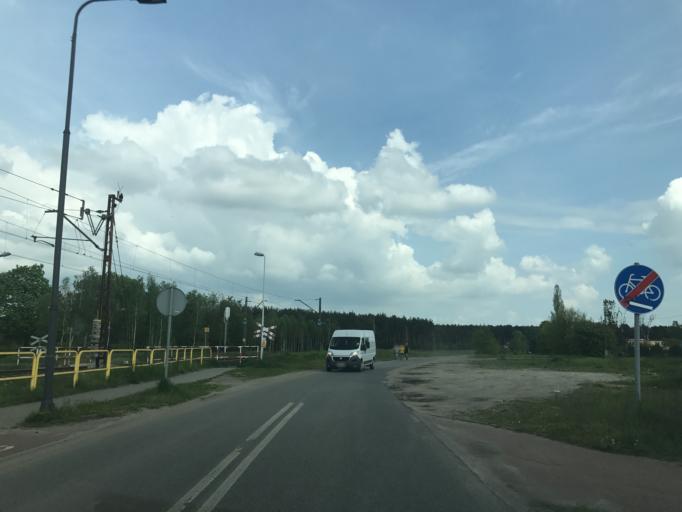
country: PL
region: Kujawsko-Pomorskie
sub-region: Bydgoszcz
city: Bydgoszcz
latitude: 53.1443
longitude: 18.0056
